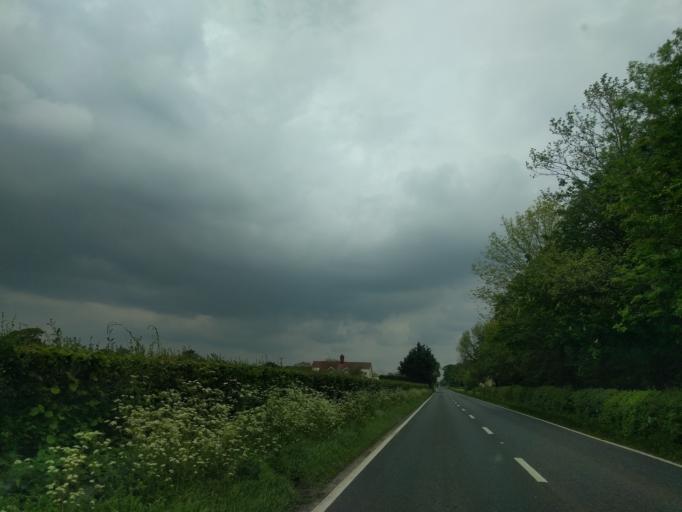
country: GB
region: England
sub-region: Somerset
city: Castle Cary
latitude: 51.0931
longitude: -2.6034
